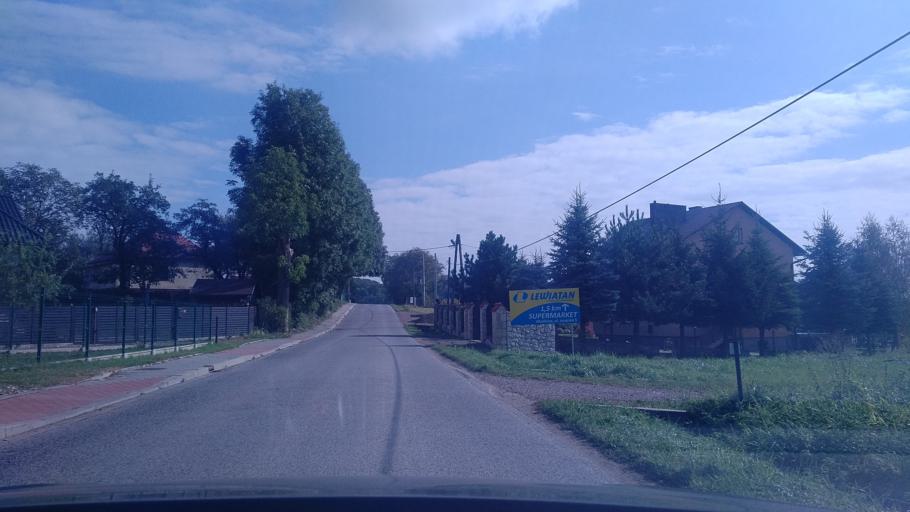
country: PL
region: Lesser Poland Voivodeship
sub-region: Powiat krakowski
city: Modlnica
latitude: 50.1342
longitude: 19.8531
